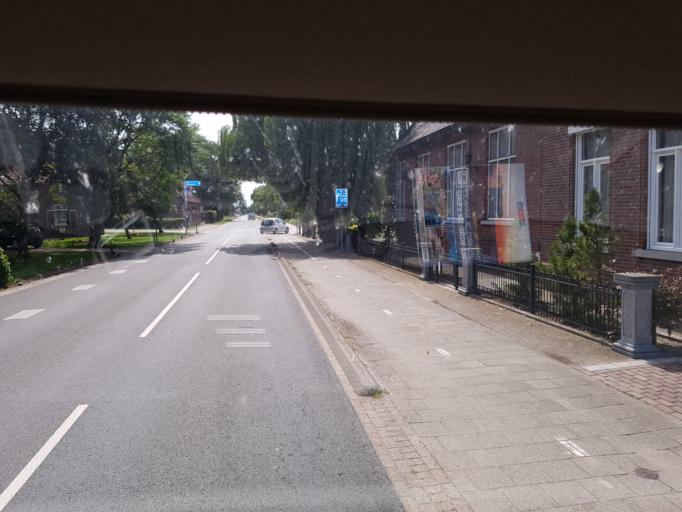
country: NL
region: Limburg
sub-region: Gemeente Leudal
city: Kelpen-Oler
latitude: 51.2298
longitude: 5.8194
